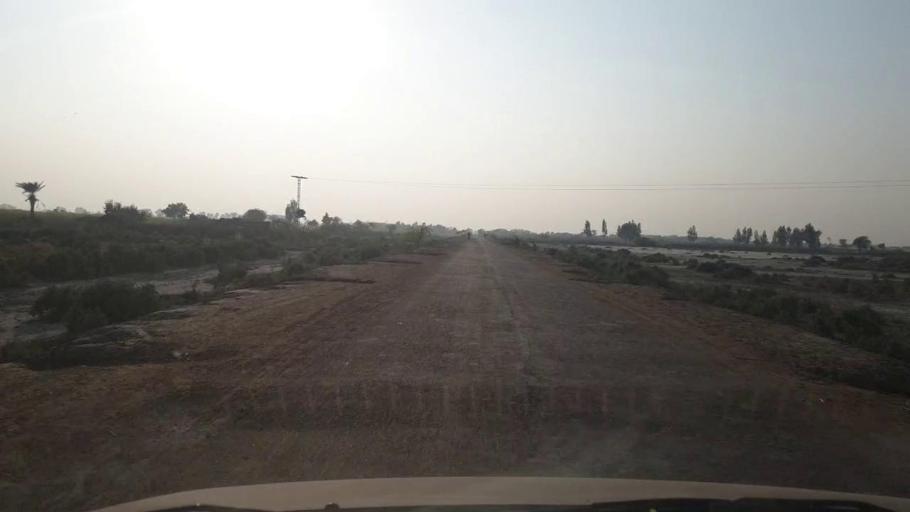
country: PK
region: Sindh
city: Mirwah Gorchani
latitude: 25.3668
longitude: 69.1616
